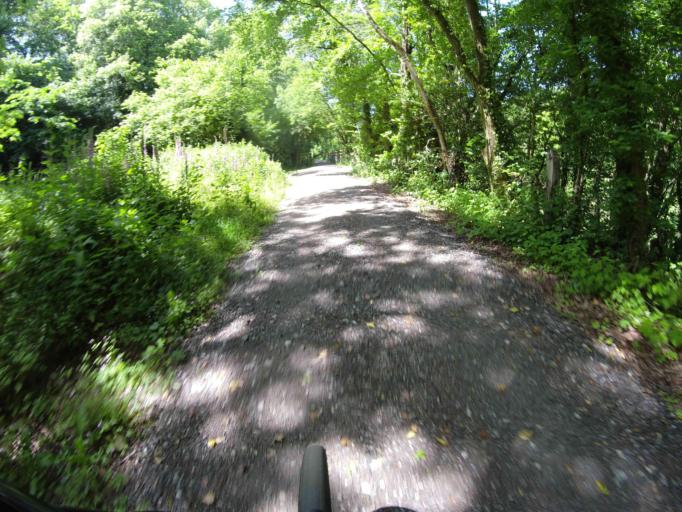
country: GB
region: England
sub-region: Devon
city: Bovey Tracey
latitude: 50.6269
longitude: -3.7175
